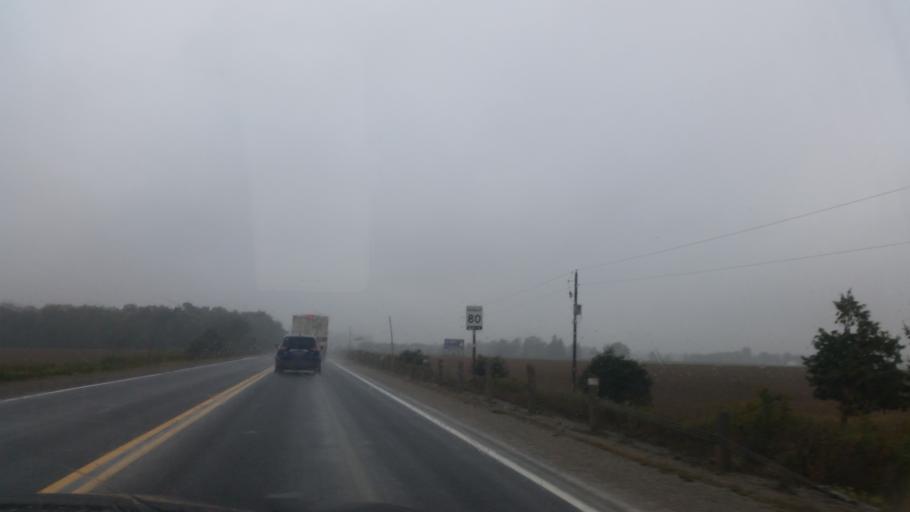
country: CA
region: Ontario
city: London
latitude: 43.2052
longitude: -81.2183
